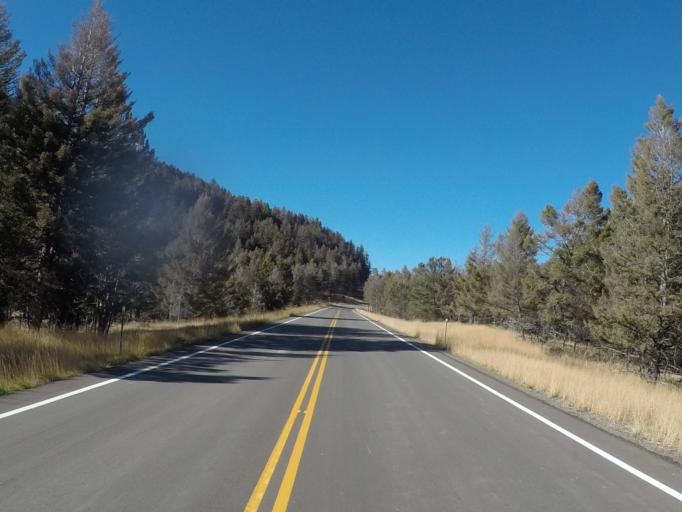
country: US
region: Montana
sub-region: Carbon County
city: Red Lodge
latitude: 44.8048
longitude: -109.4467
